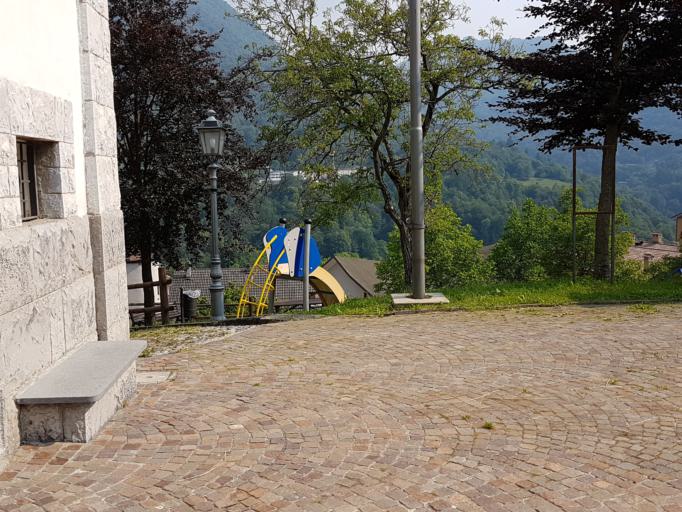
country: IT
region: Lombardy
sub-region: Provincia di Lecco
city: Esino Lario
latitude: 45.9943
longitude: 9.3306
